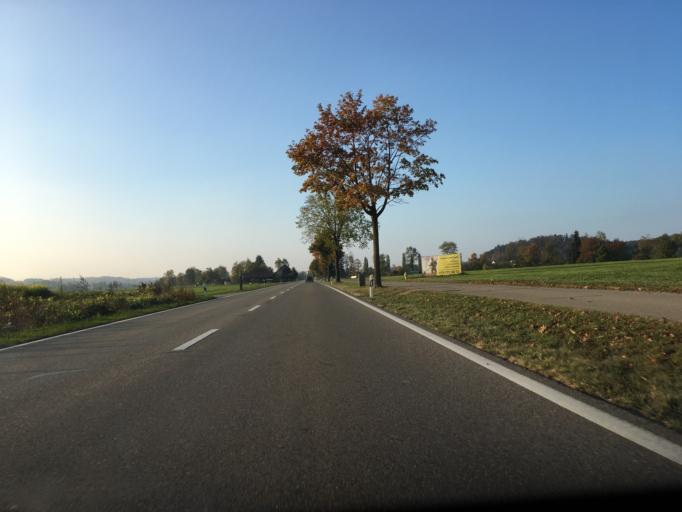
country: CH
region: Zurich
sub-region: Bezirk Pfaeffikon
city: Pfaeffikon / Pfaeffikon (Dorfkern)
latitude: 47.3768
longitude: 8.7681
